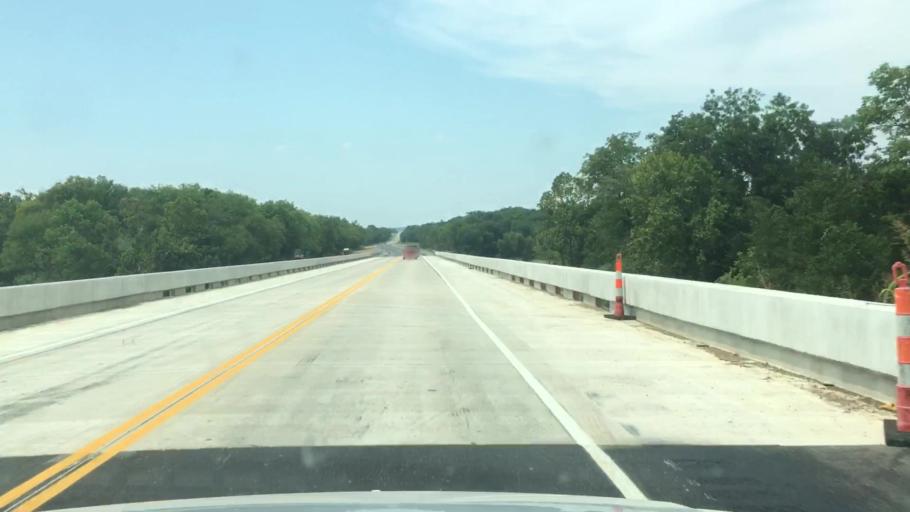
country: US
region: Oklahoma
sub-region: Muskogee County
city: Fort Gibson
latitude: 35.9370
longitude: -95.1759
